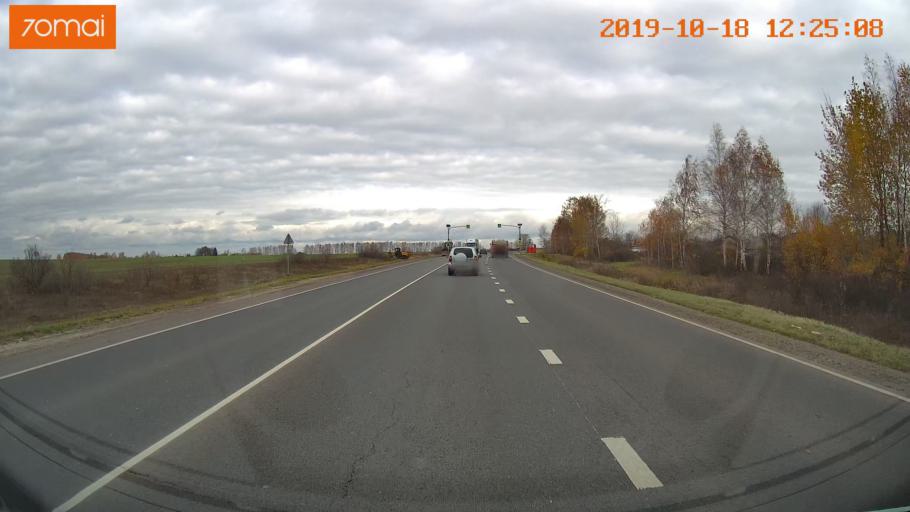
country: RU
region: Rjazan
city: Rybnoye
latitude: 54.5463
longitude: 39.5170
